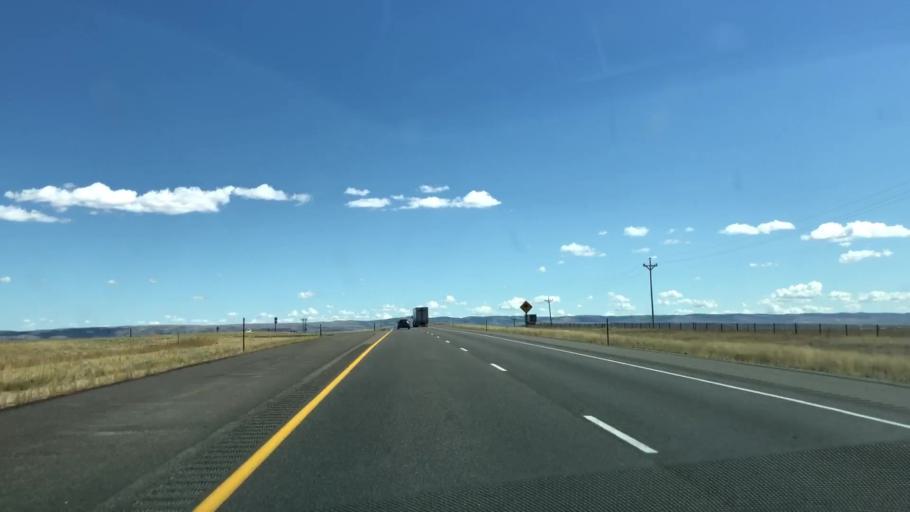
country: US
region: Wyoming
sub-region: Albany County
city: Laramie
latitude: 41.3493
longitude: -105.7099
